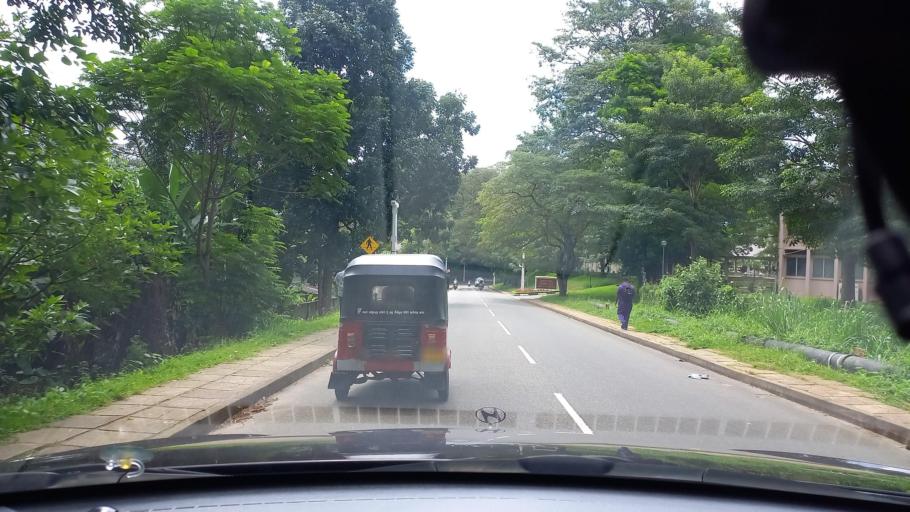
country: LK
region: Central
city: Kandy
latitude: 7.2624
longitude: 80.5989
